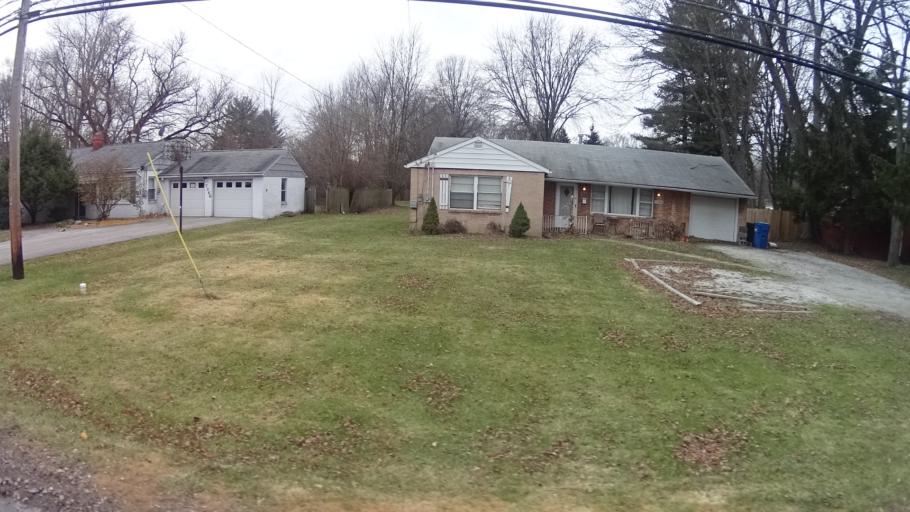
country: US
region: Ohio
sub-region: Lorain County
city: North Ridgeville
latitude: 41.3855
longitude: -82.0186
